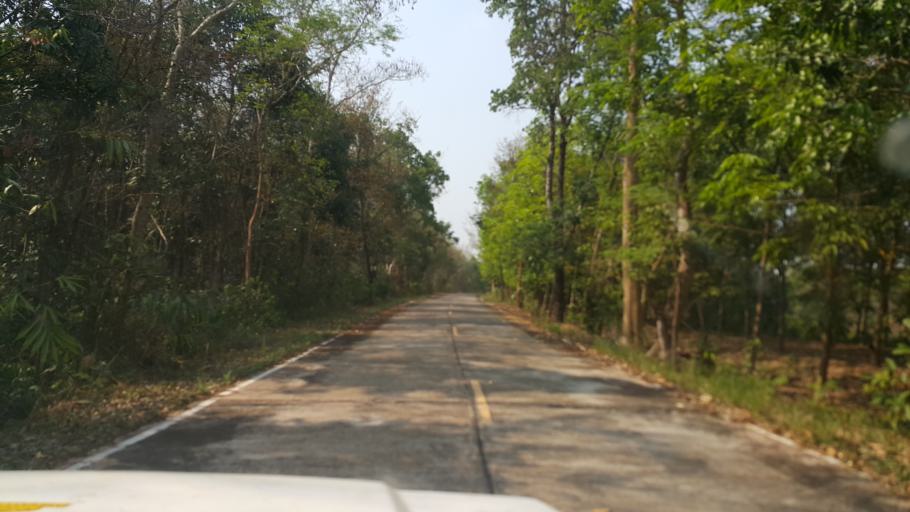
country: TH
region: Nakhon Phanom
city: Ban Phaeng
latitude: 17.9714
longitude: 104.1520
